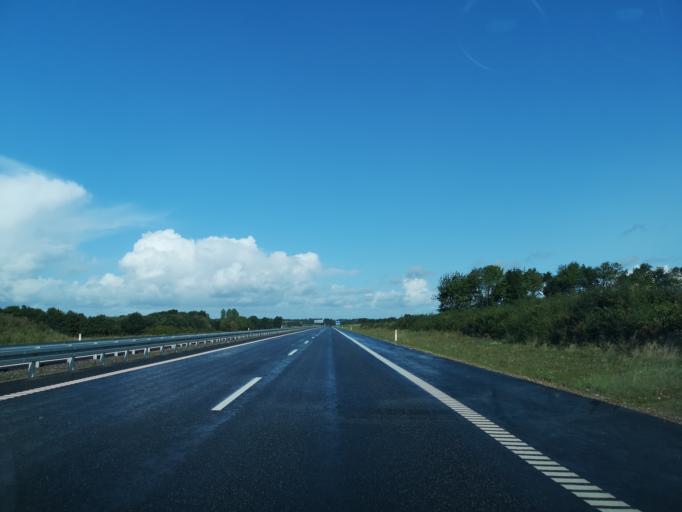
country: DK
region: Central Jutland
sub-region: Herning Kommune
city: Snejbjerg
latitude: 56.2033
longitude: 8.8747
